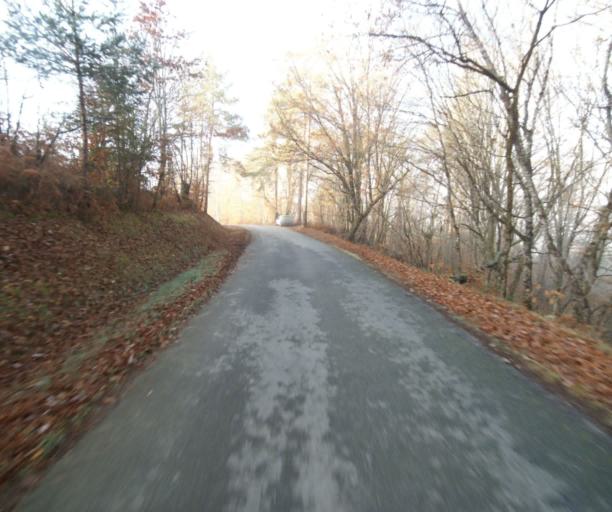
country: FR
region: Limousin
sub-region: Departement de la Correze
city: Laguenne
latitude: 45.2619
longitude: 1.7933
